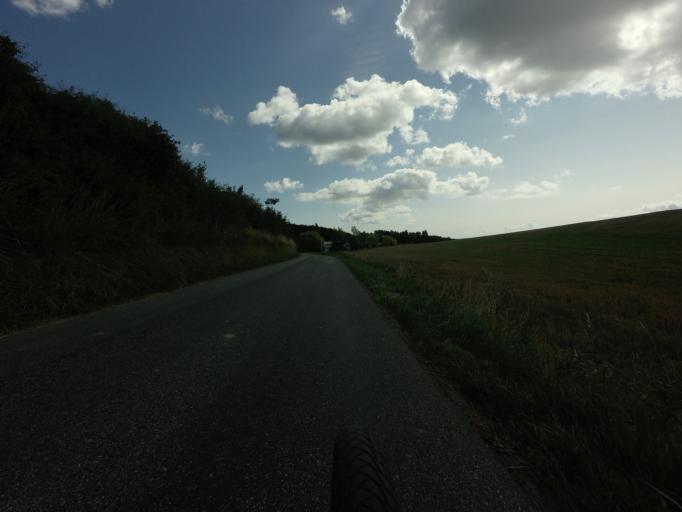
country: DK
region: Zealand
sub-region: Vordingborg Kommune
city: Stege
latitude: 54.9593
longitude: 12.5290
